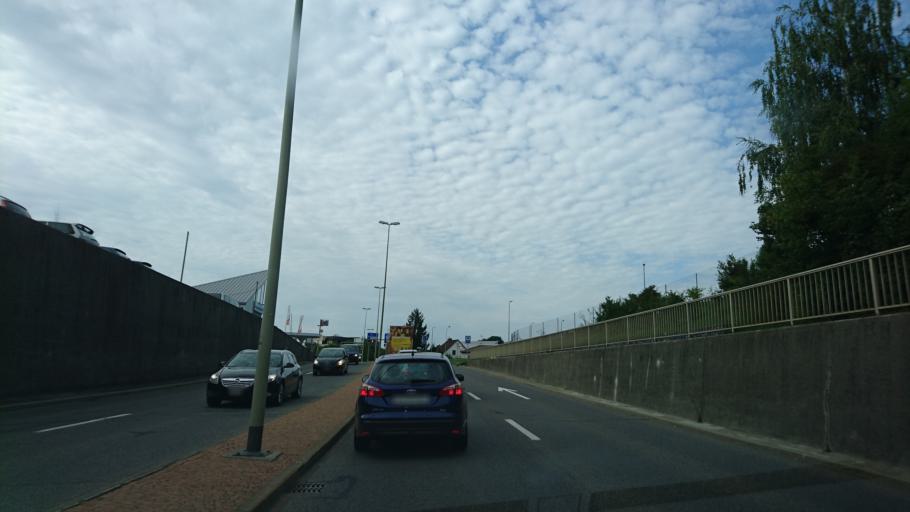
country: CH
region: Zurich
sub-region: Bezirk Hinwil
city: Hinwil
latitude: 47.3027
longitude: 8.8340
